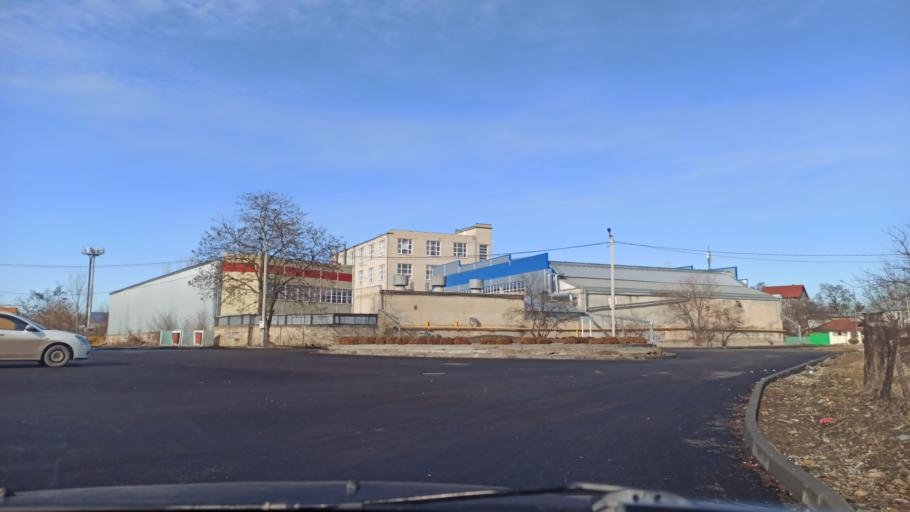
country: RU
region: Stavropol'skiy
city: Yessentukskaya
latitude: 44.0365
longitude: 42.8749
